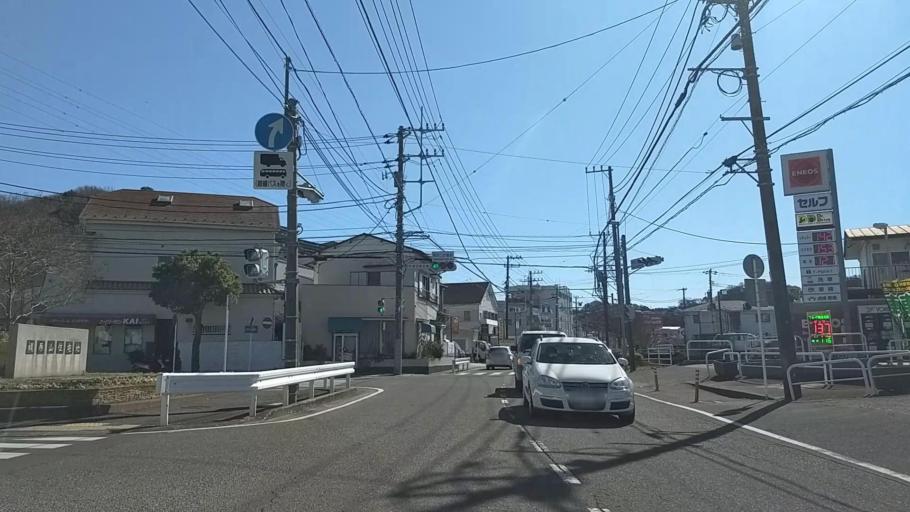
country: JP
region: Kanagawa
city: Kamakura
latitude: 35.3268
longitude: 139.5238
